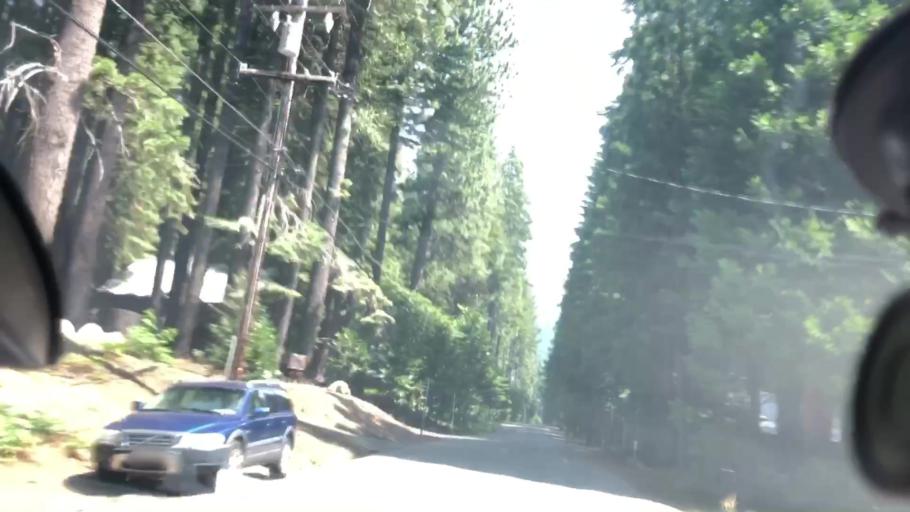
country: US
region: California
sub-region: El Dorado County
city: South Lake Tahoe
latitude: 38.7998
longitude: -120.1455
